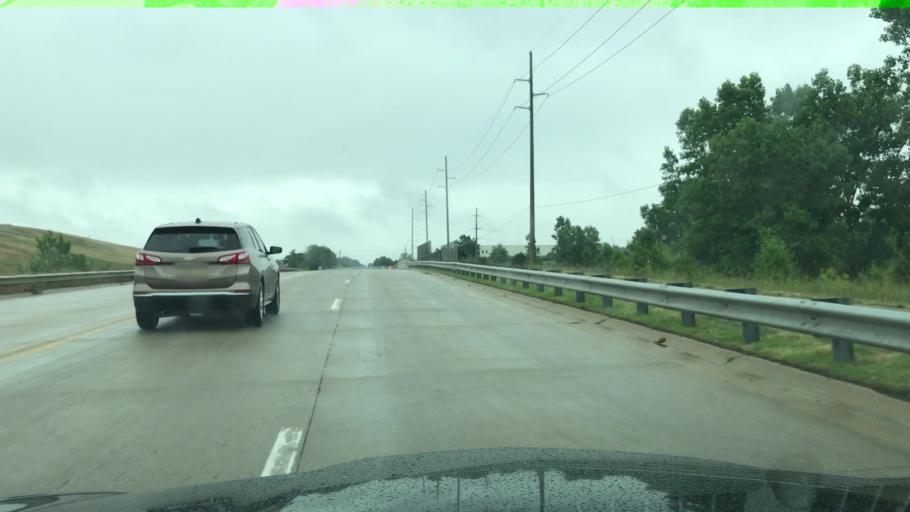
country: US
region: Michigan
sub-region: Oakland County
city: Auburn Hills
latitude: 42.7226
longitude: -83.2582
